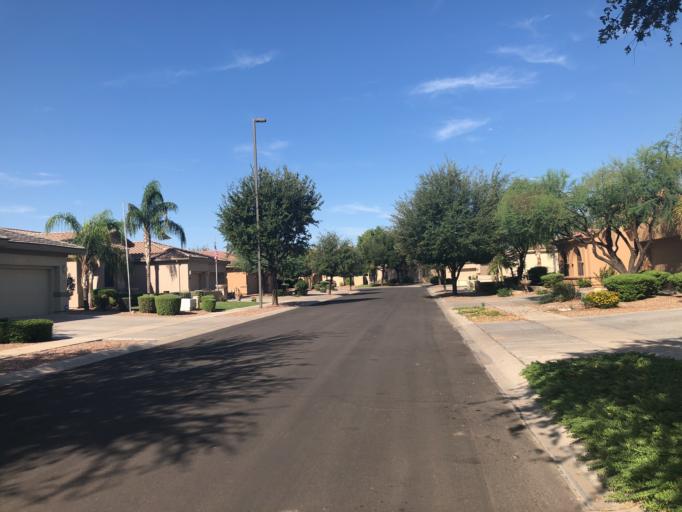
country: US
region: Arizona
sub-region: Maricopa County
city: Queen Creek
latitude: 33.2673
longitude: -111.6905
